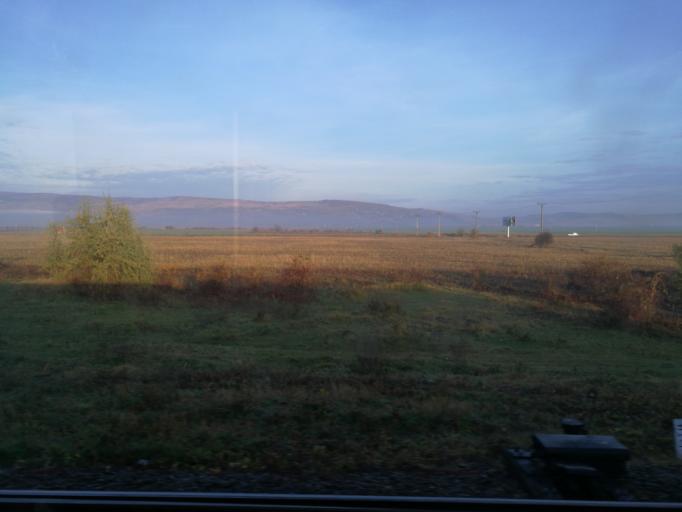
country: RO
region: Buzau
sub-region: Comuna Ulmeni
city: Ulmeni
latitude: 45.0834
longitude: 26.6572
